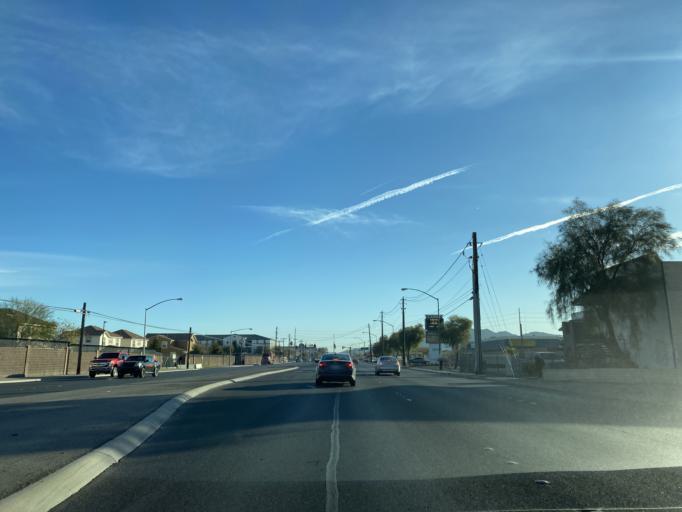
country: US
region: Nevada
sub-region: Clark County
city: Nellis Air Force Base
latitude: 36.2404
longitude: -115.0647
